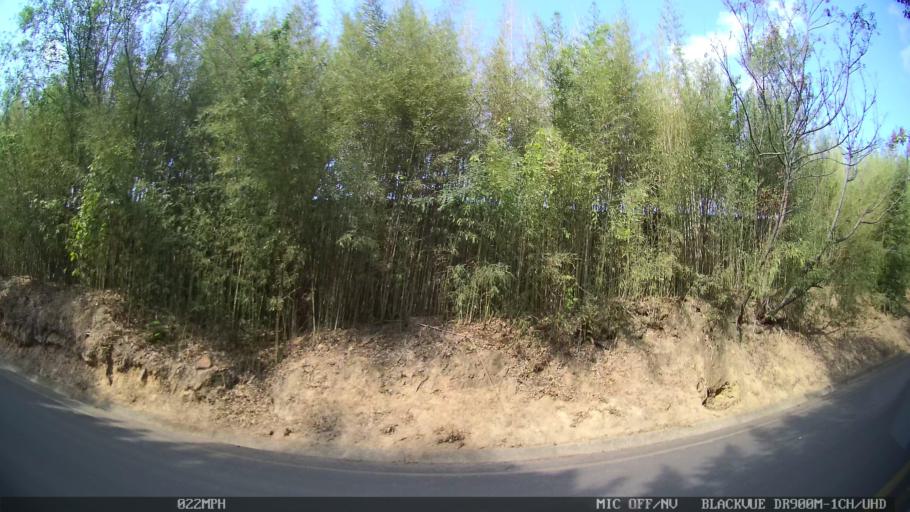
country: BR
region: Sao Paulo
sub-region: Indaiatuba
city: Indaiatuba
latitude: -22.9939
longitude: -47.1915
